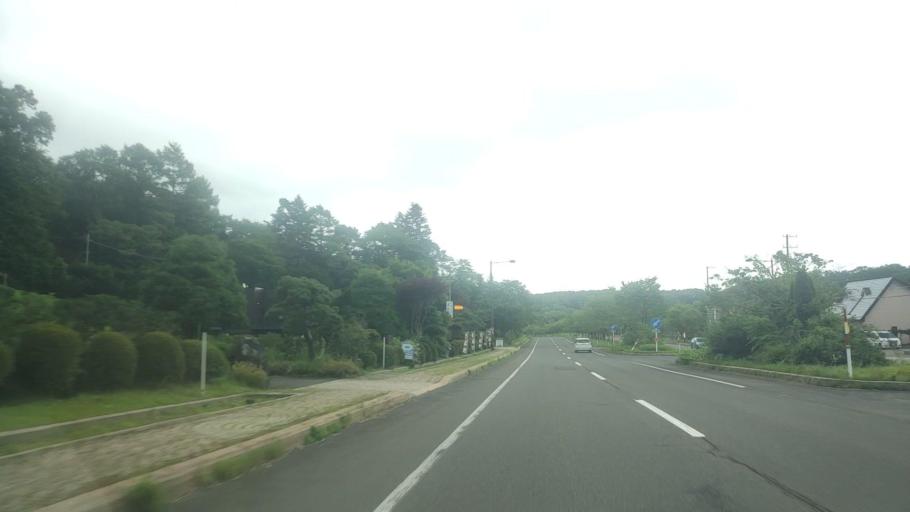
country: JP
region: Hokkaido
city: Shiraoi
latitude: 42.4660
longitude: 141.1689
